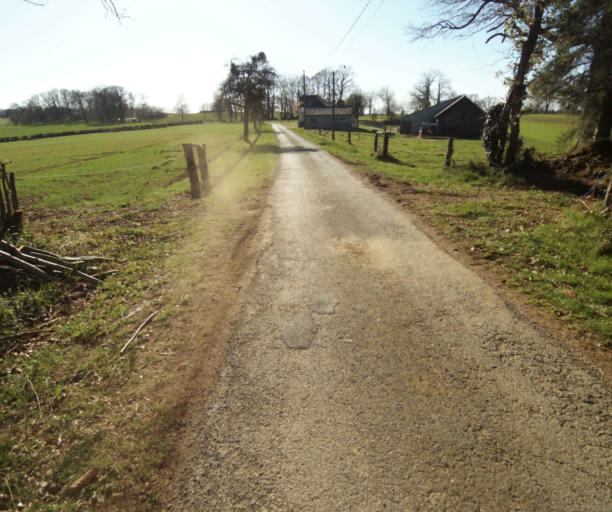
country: FR
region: Limousin
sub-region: Departement de la Correze
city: Seilhac
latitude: 45.3912
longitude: 1.6890
